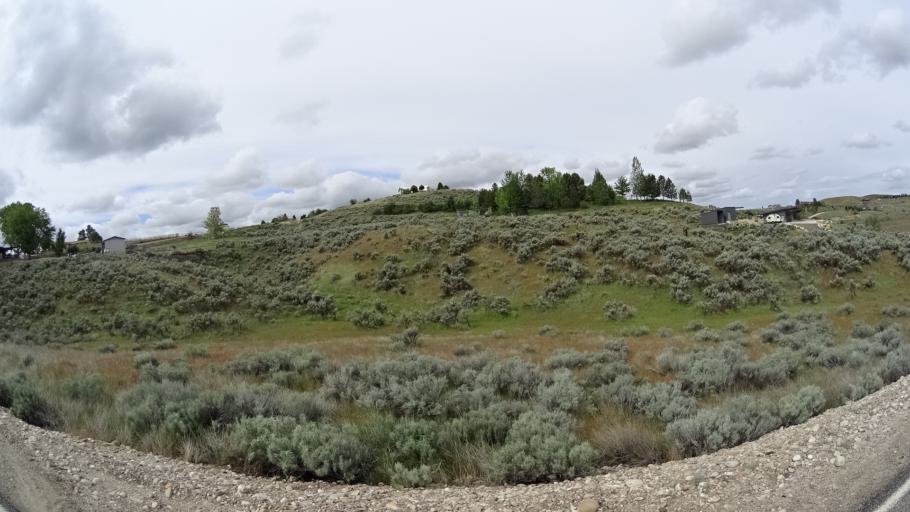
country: US
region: Idaho
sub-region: Ada County
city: Eagle
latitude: 43.7423
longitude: -116.3568
